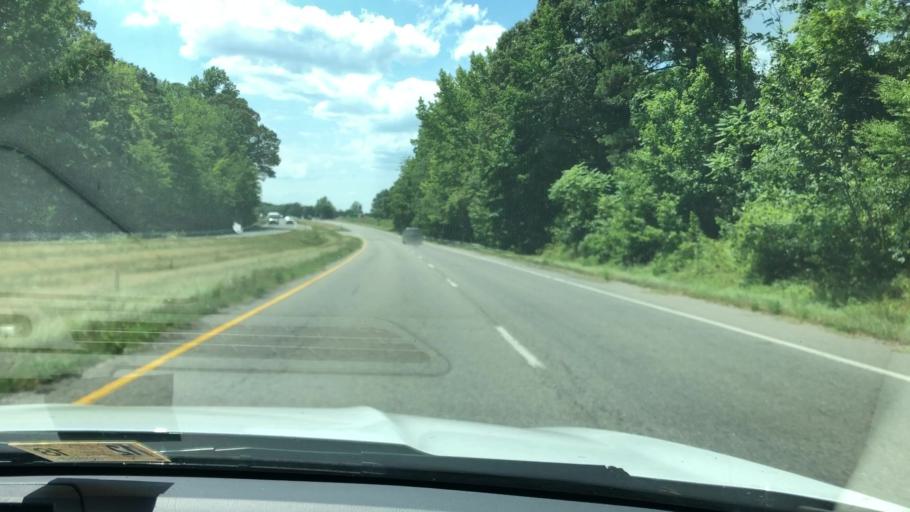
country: US
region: Virginia
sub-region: King William County
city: West Point
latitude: 37.5487
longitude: -76.7283
